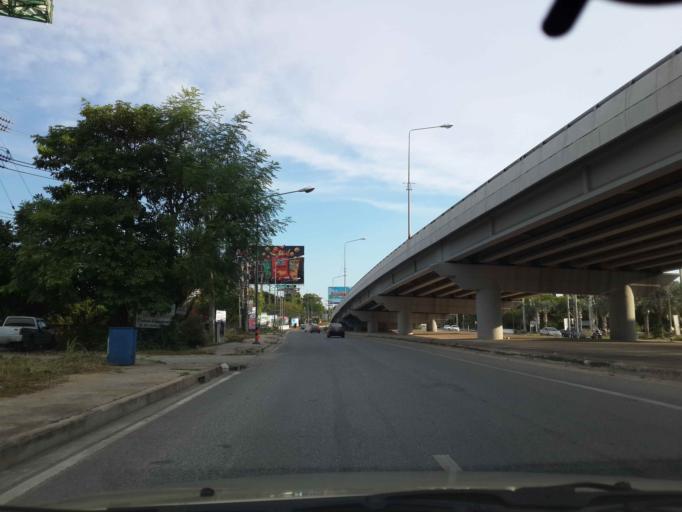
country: TH
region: Chon Buri
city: Bang Lamung
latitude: 13.0008
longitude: 100.9299
